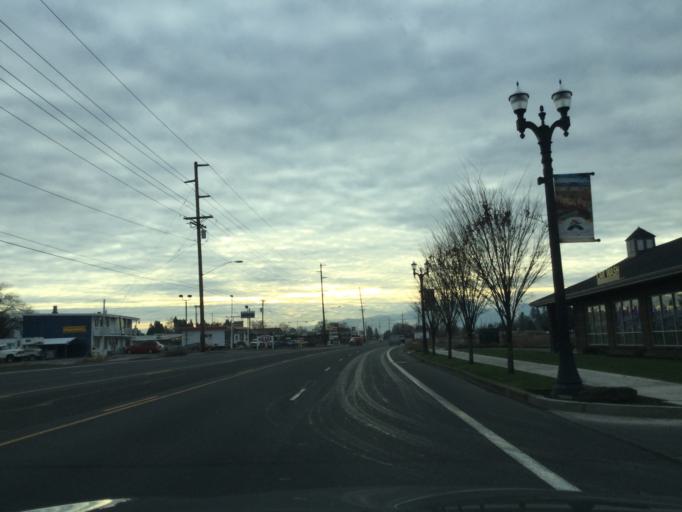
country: US
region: Oregon
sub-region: Jackson County
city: Central Point
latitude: 42.3709
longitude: -122.9153
